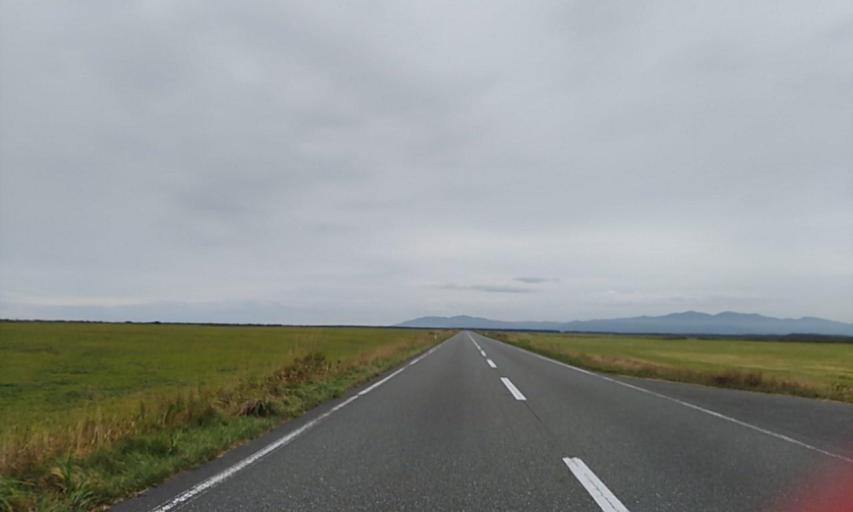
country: JP
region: Hokkaido
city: Makubetsu
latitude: 45.1879
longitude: 142.3145
